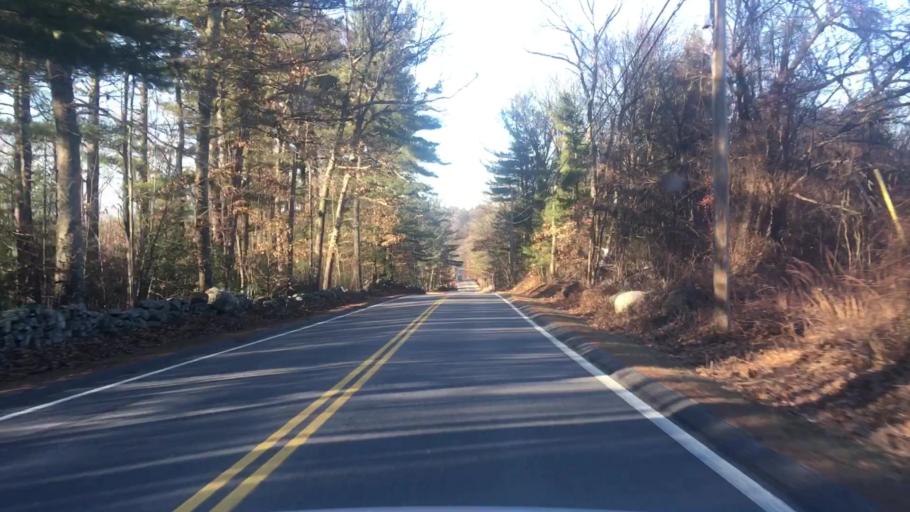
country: US
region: New Hampshire
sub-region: Rockingham County
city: Londonderry
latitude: 42.8922
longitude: -71.3699
